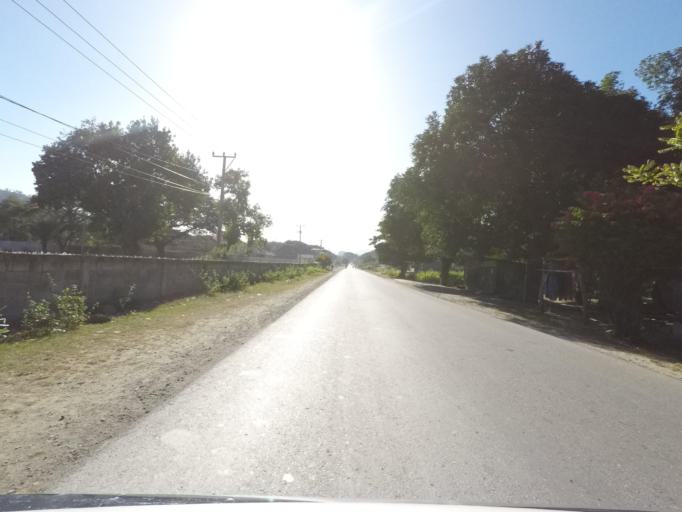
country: TL
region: Dili
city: Dili
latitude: -8.5570
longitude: 125.6487
